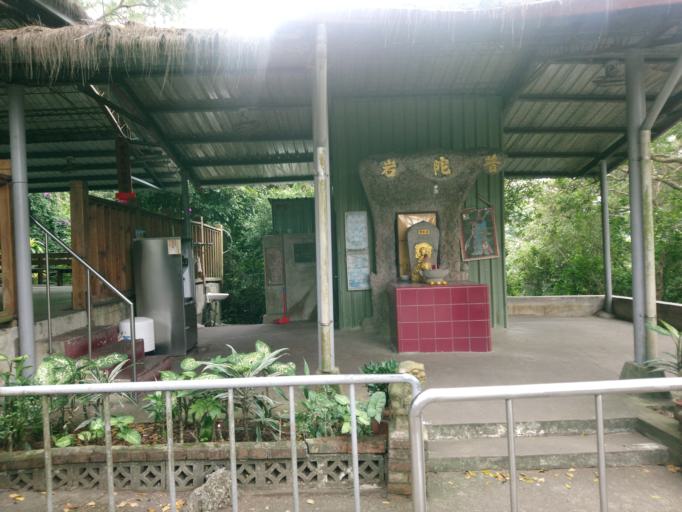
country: TW
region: Taiwan
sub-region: Hsinchu
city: Hsinchu
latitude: 24.7906
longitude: 120.9818
